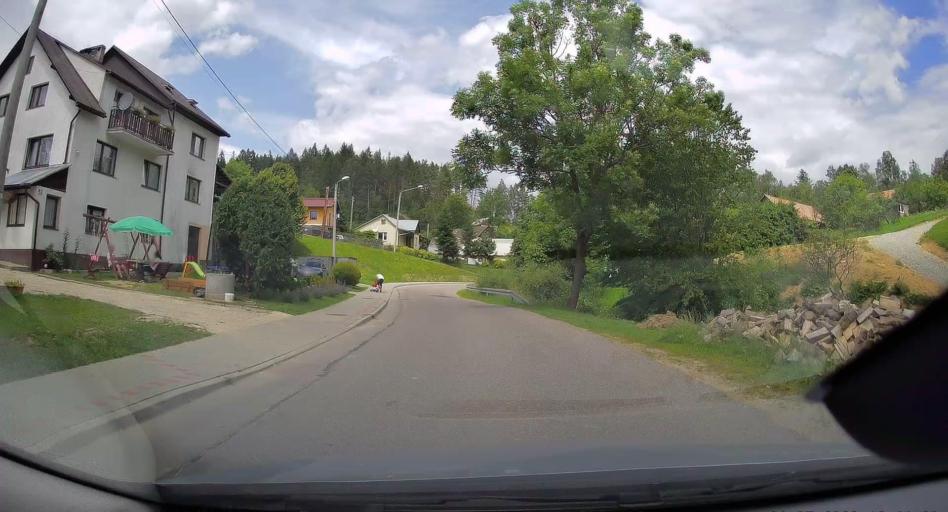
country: PL
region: Lesser Poland Voivodeship
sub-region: Powiat nowosadecki
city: Muszyna
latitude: 49.3811
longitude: 20.8956
